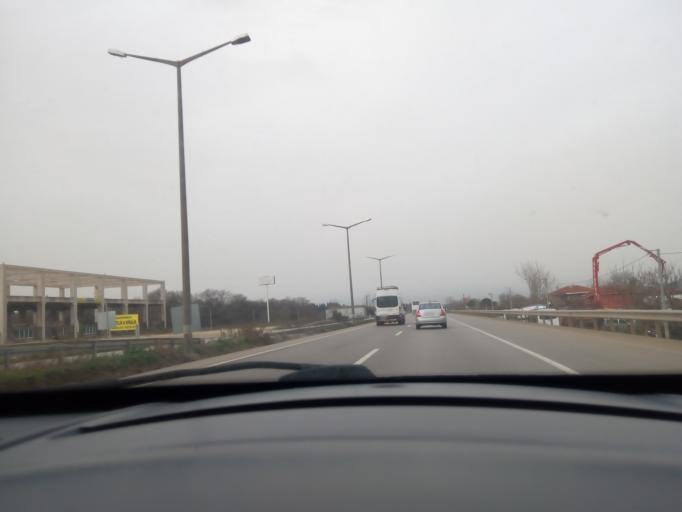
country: TR
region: Bursa
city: Tatkavakli
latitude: 40.0324
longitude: 28.3651
